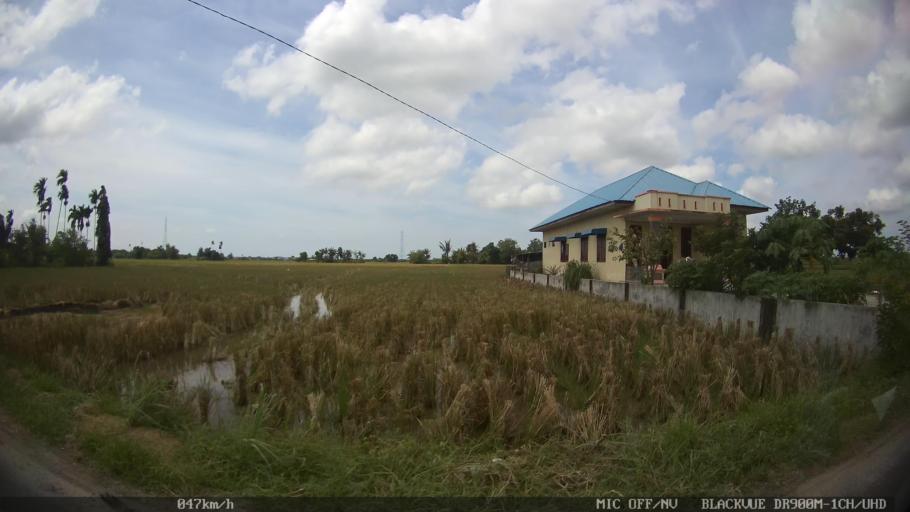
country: ID
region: North Sumatra
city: Percut
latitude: 3.5720
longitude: 98.8450
